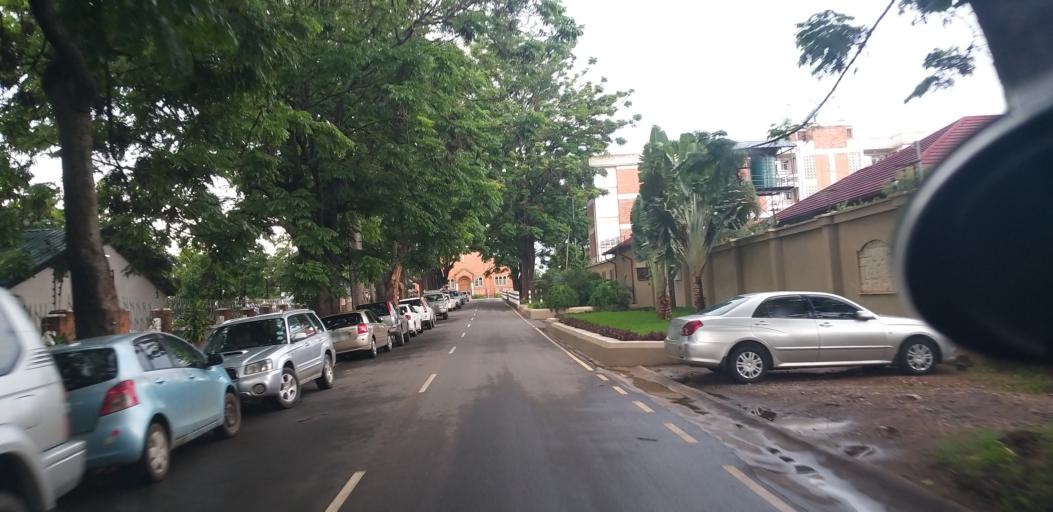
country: ZM
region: Lusaka
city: Lusaka
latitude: -15.4144
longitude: 28.2983
